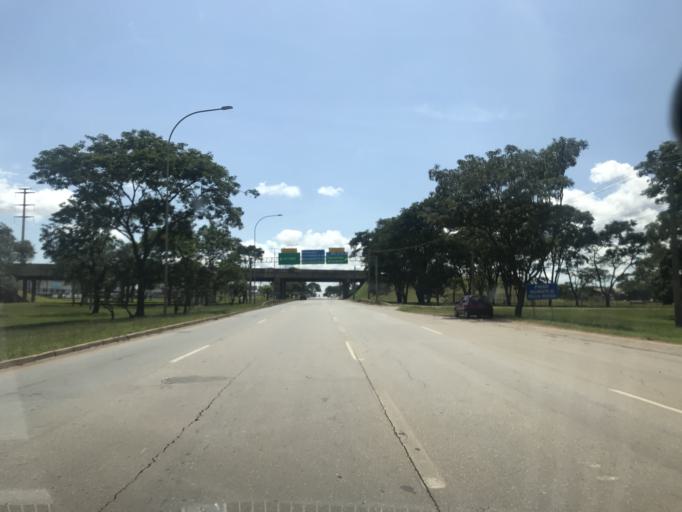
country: BR
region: Federal District
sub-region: Brasilia
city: Brasilia
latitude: -15.8760
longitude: -48.0292
